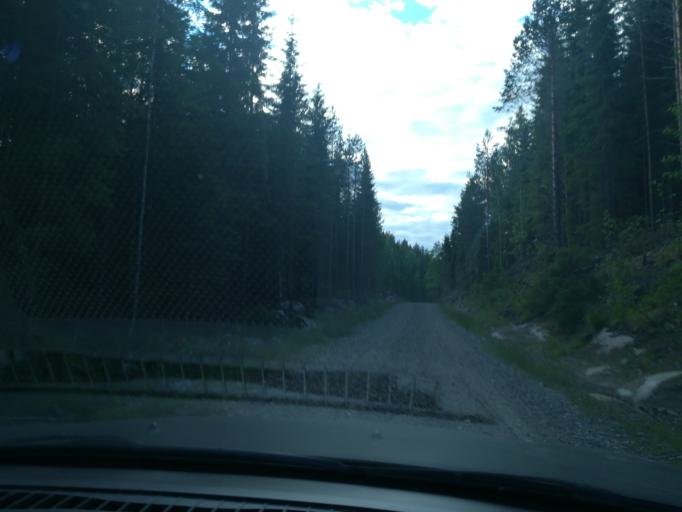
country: FI
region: Southern Savonia
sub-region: Mikkeli
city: Puumala
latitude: 61.6212
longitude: 28.1728
